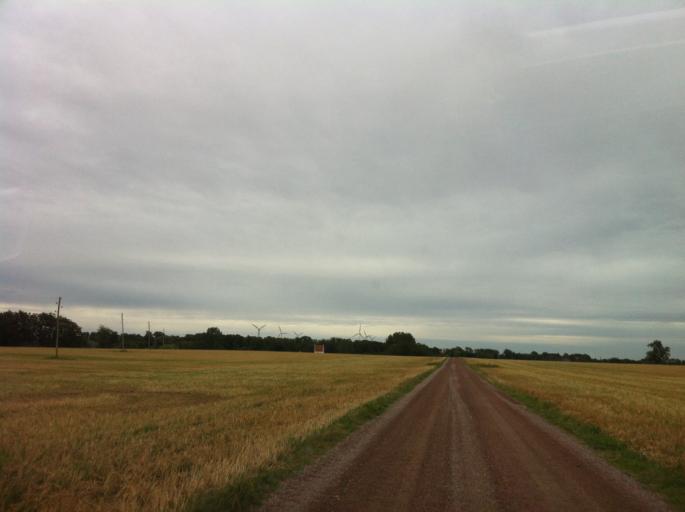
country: SE
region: Skane
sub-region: Landskrona
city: Asmundtorp
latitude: 55.9342
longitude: 12.9933
